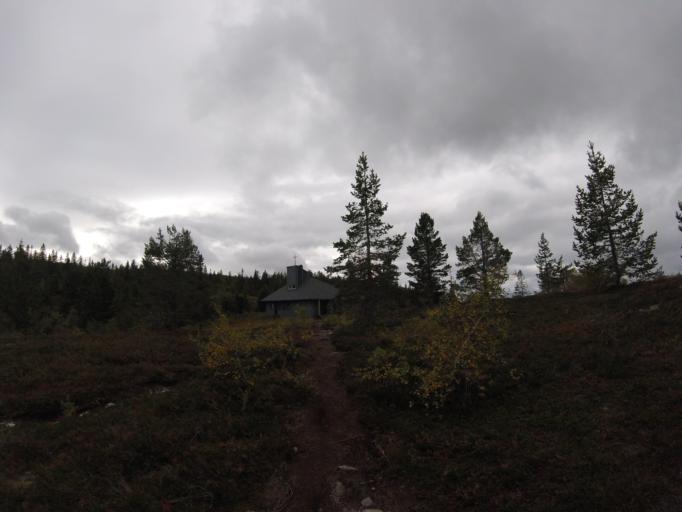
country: NO
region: Buskerud
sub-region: Flesberg
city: Lampeland
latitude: 59.7551
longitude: 9.4133
